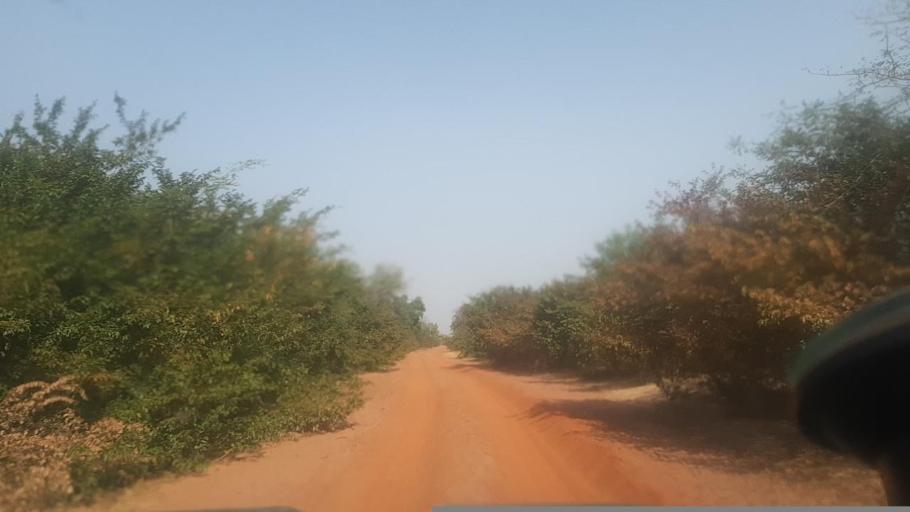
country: ML
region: Segou
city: Bla
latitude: 12.8531
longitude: -5.9809
